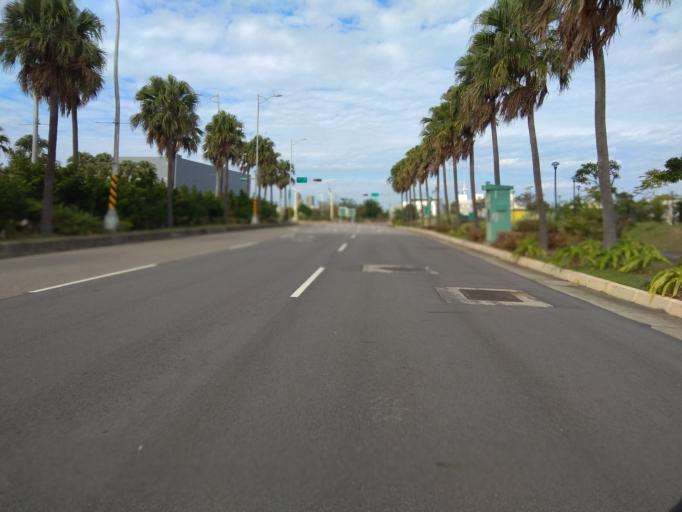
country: TW
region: Taiwan
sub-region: Hsinchu
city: Zhubei
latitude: 25.0340
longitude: 121.0720
